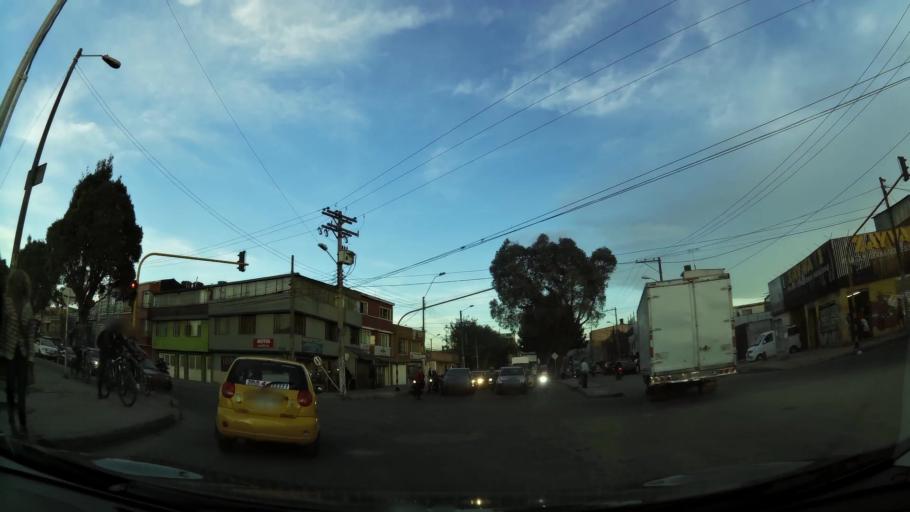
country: CO
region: Cundinamarca
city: Funza
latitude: 4.6832
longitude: -74.1359
